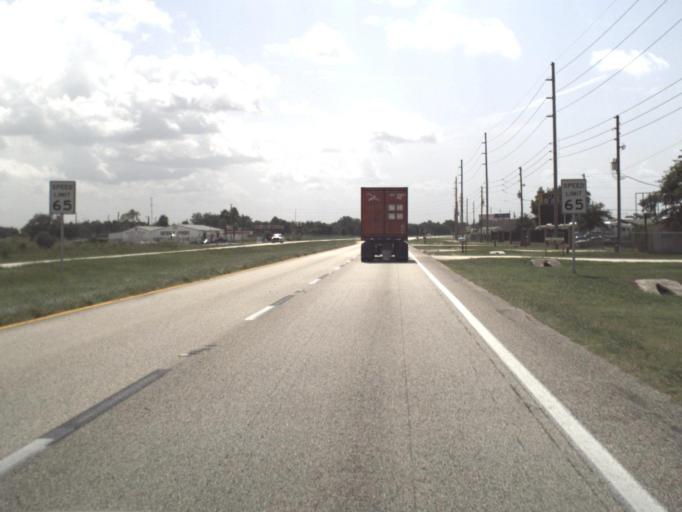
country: US
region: Florida
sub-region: Polk County
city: Crooked Lake Park
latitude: 27.8598
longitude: -81.5885
